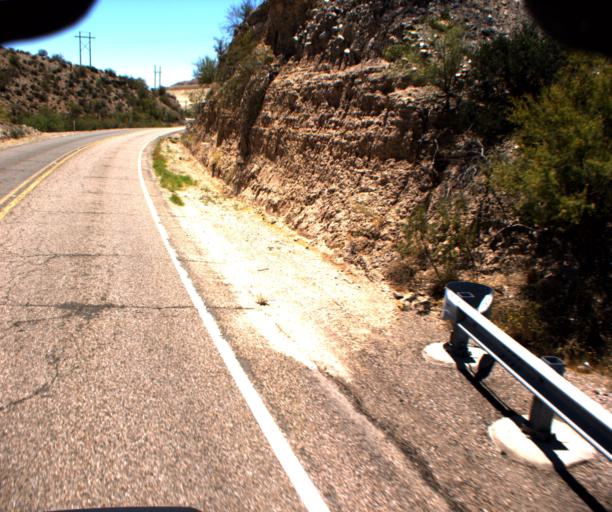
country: US
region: Arizona
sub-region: Pinal County
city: Kearny
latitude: 33.0077
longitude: -110.8010
